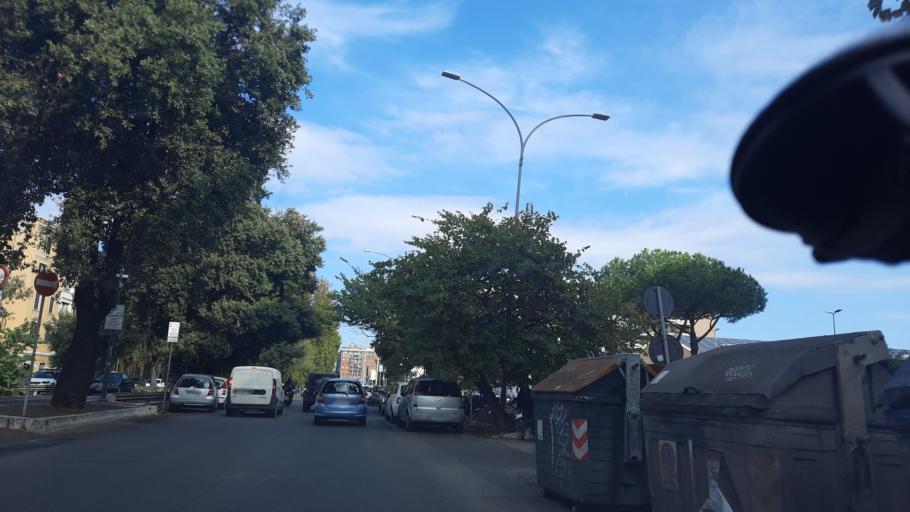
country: IT
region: Latium
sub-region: Citta metropolitana di Roma Capitale
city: Rome
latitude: 41.8654
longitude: 12.4796
